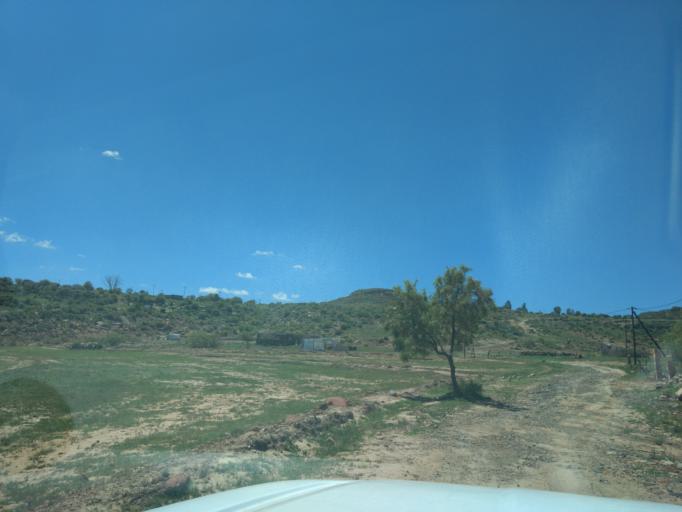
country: LS
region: Maseru
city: Maseru
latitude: -29.4613
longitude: 27.3724
